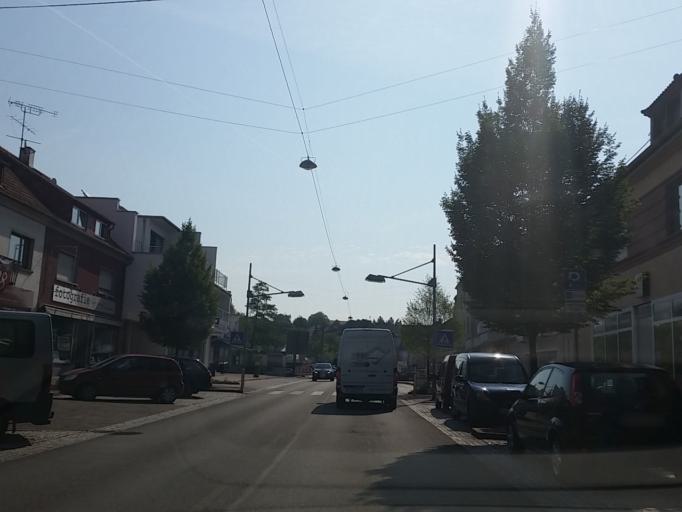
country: DE
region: Saarland
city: Schmelz
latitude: 49.4424
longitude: 6.8529
